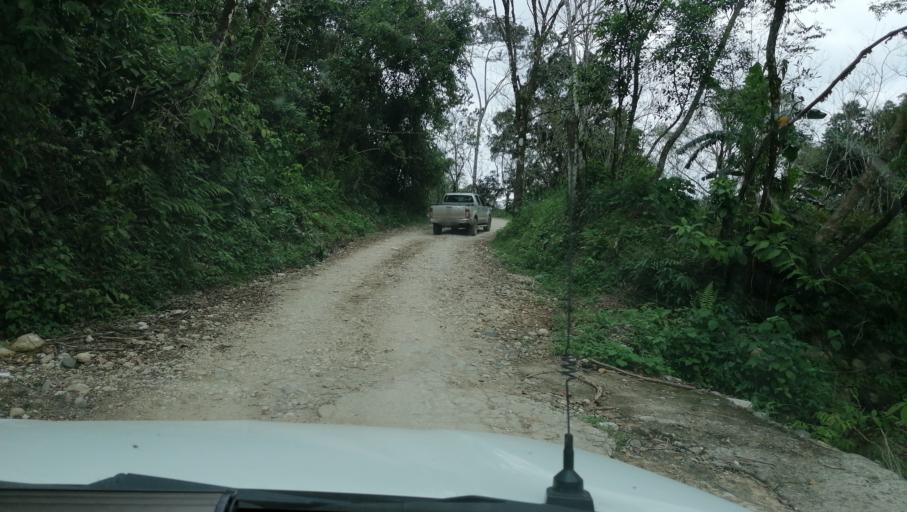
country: MX
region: Chiapas
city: Ocotepec
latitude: 17.2746
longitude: -93.2230
